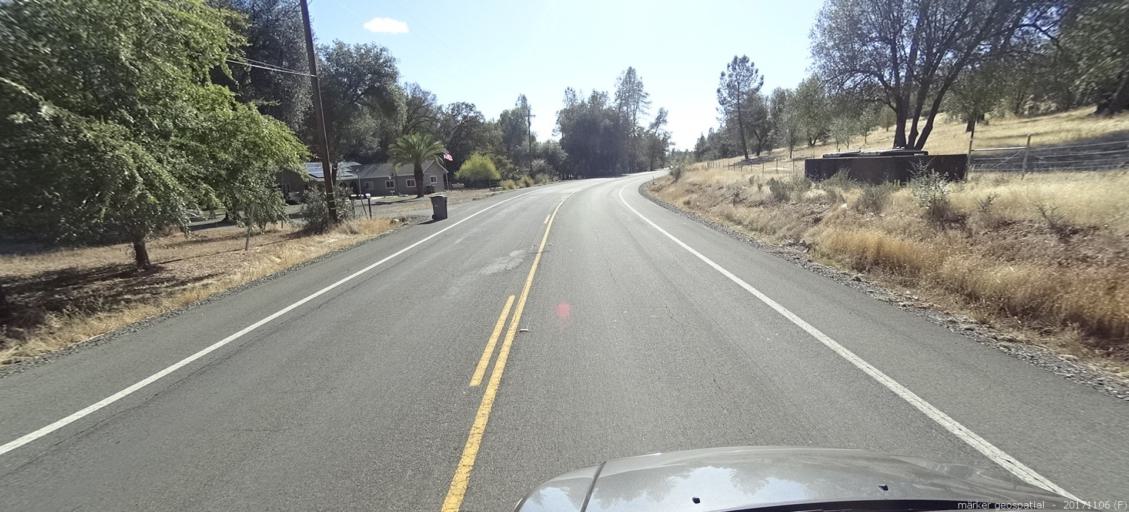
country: US
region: California
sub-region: Shasta County
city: Redding
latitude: 40.6124
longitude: -122.3170
